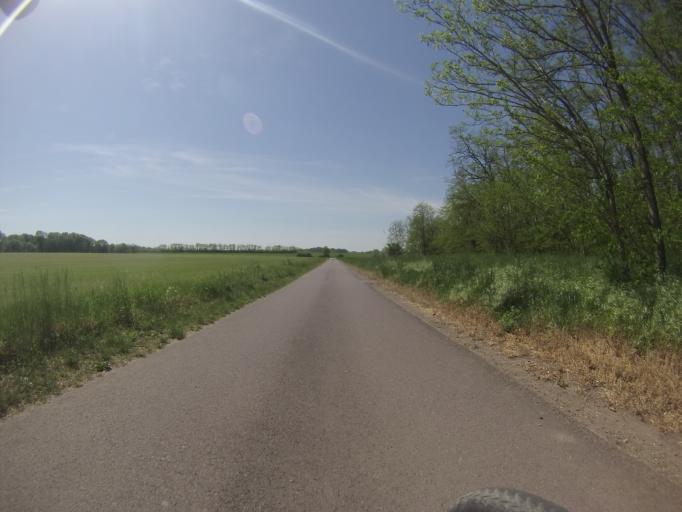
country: CZ
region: South Moravian
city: Novosedly
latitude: 48.8037
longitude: 16.4909
